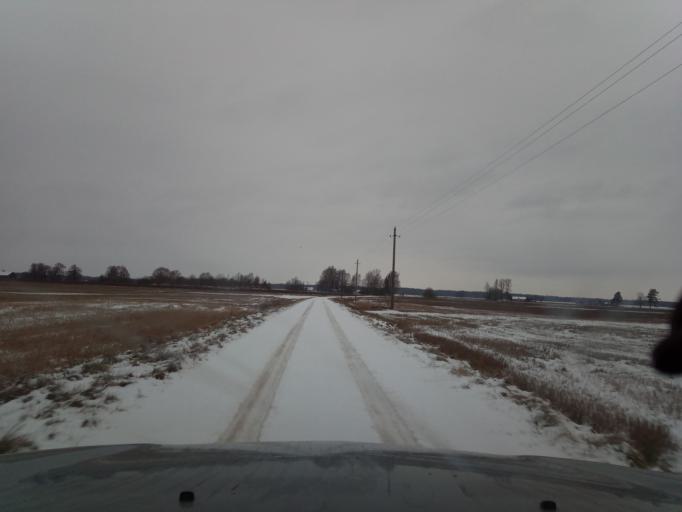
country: LT
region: Vilnius County
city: Ukmerge
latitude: 55.4834
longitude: 24.6003
